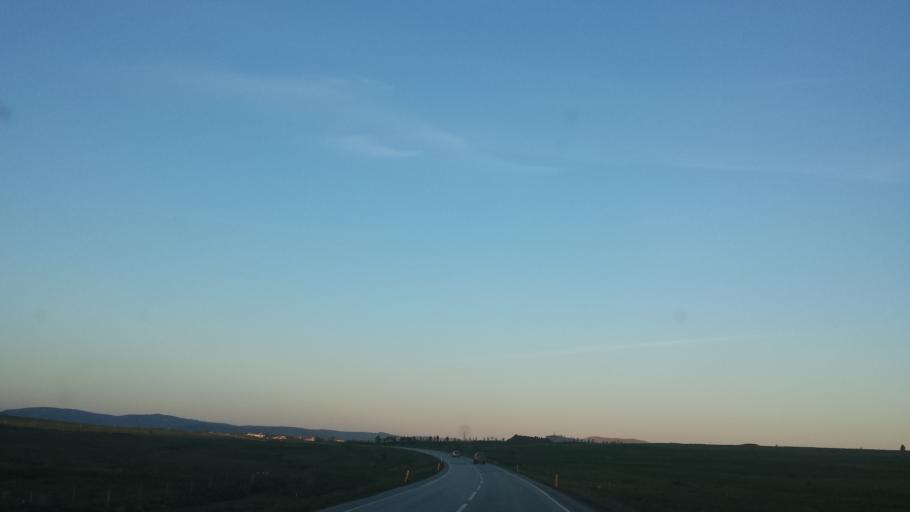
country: IS
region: Capital Region
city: Reykjavik
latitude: 64.2244
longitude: -21.8109
